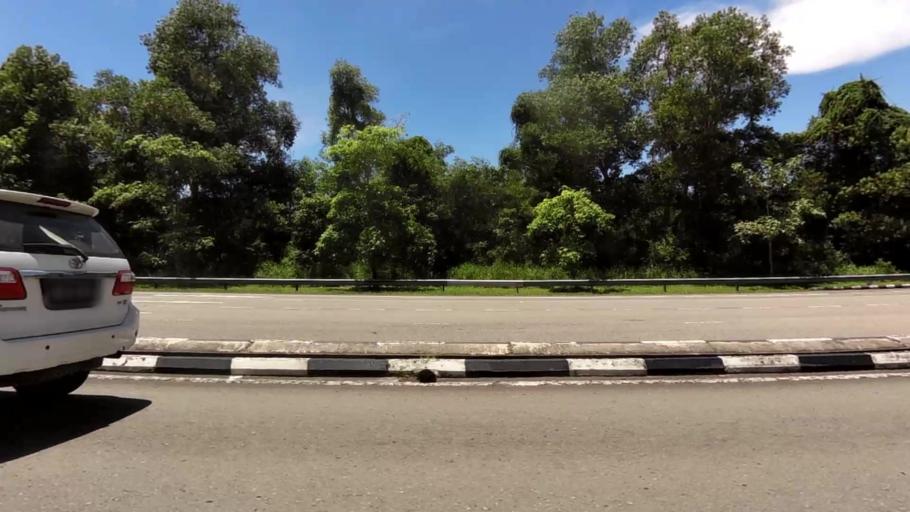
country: BN
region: Brunei and Muara
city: Bandar Seri Begawan
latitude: 4.9179
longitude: 114.9523
